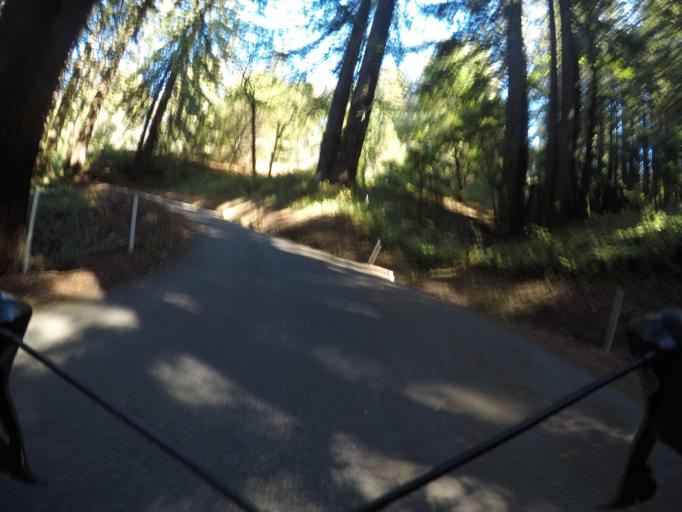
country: US
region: California
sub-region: San Mateo County
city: Portola Valley
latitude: 37.3676
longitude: -122.2562
